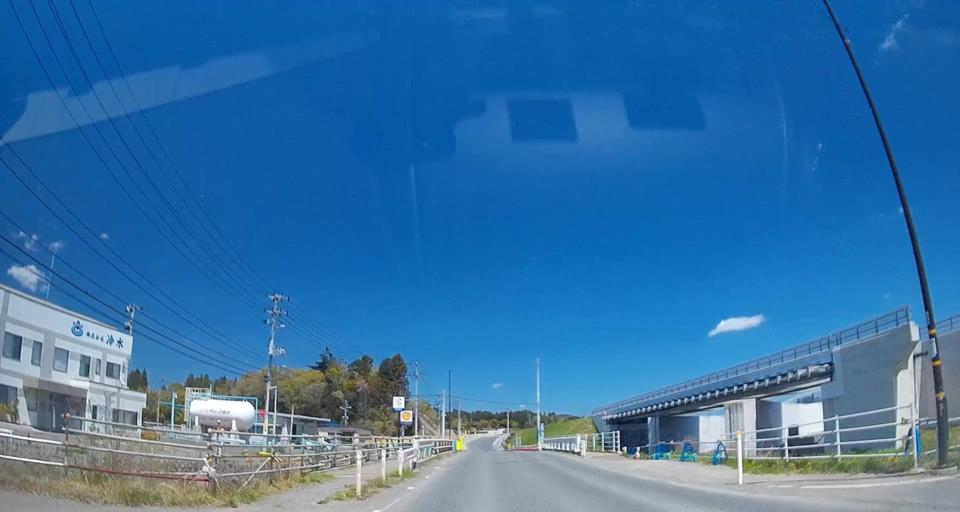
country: JP
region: Iwate
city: Ofunato
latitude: 38.8701
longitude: 141.5820
